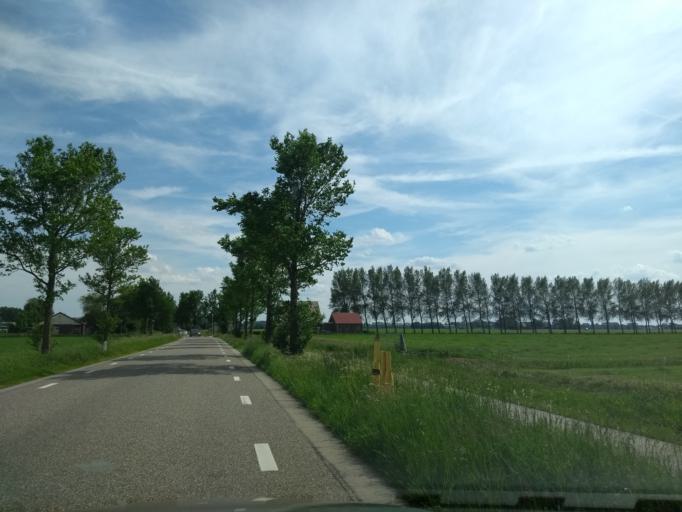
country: NL
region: Groningen
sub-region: Gemeente Zuidhorn
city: Noordhorn
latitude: 53.2785
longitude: 6.4236
